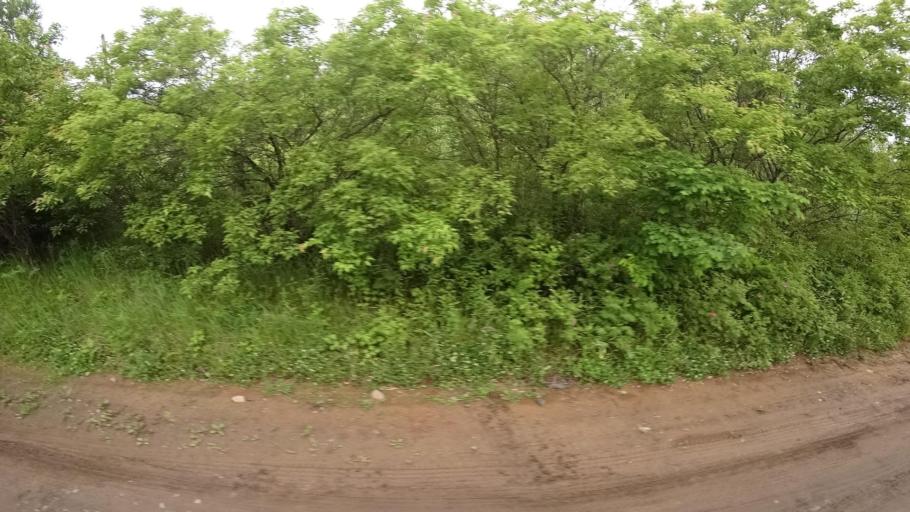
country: RU
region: Khabarovsk Krai
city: Amursk
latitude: 49.8862
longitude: 136.1279
